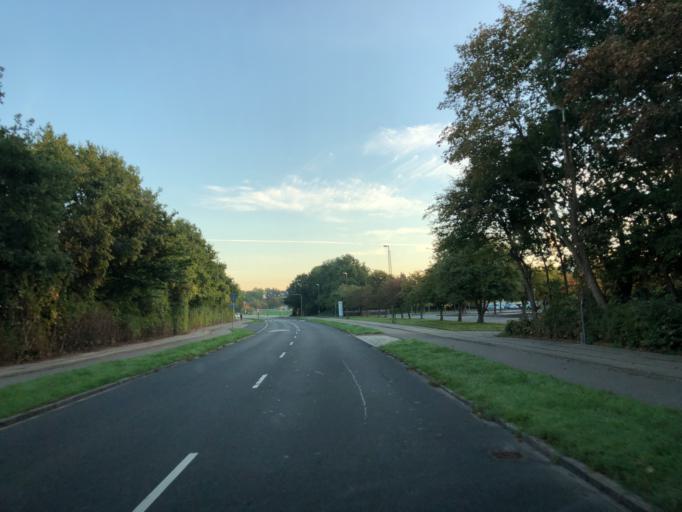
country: DK
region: South Denmark
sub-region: Sonderborg Kommune
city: Sonderborg
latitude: 54.8984
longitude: 9.8082
